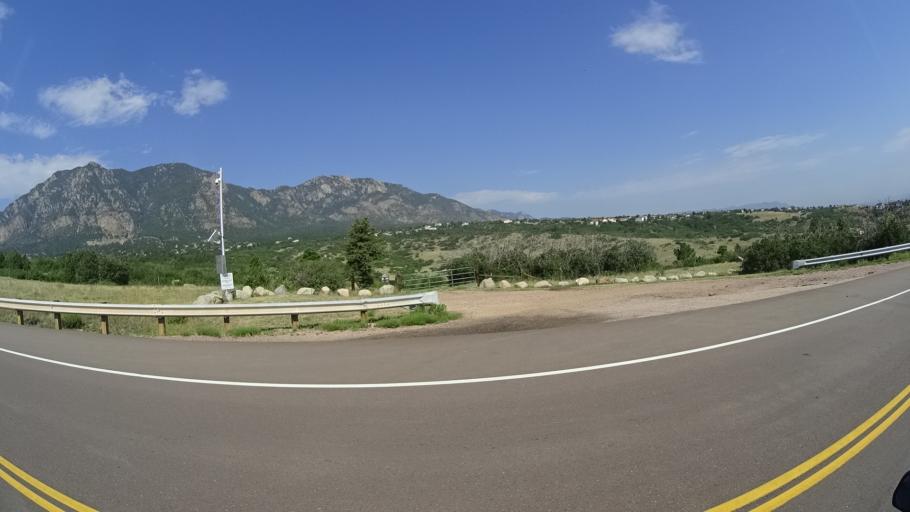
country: US
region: Colorado
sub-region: El Paso County
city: Fort Carson
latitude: 38.7497
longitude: -104.8197
